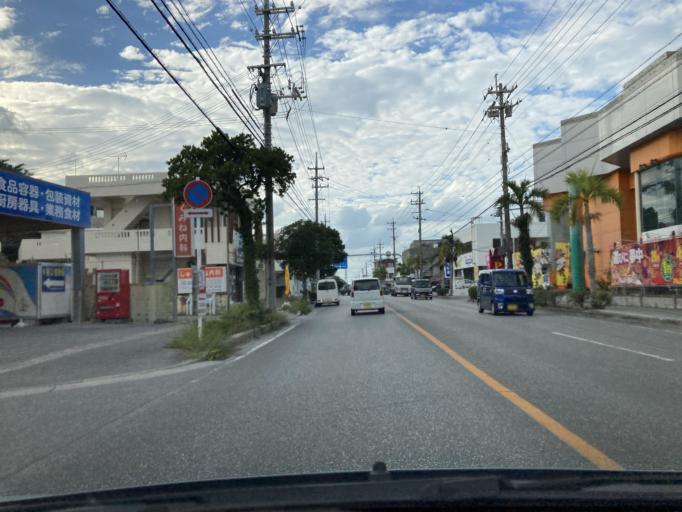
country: JP
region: Okinawa
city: Okinawa
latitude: 26.3596
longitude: 127.8222
